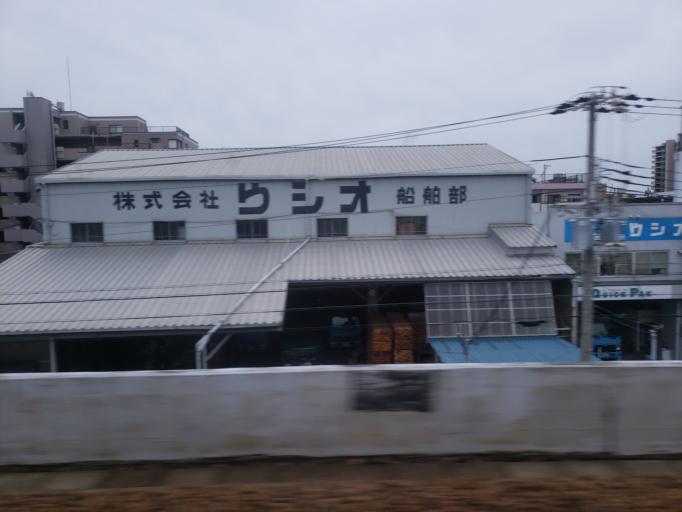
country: JP
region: Hyogo
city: Kobe
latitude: 34.6726
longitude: 135.1722
